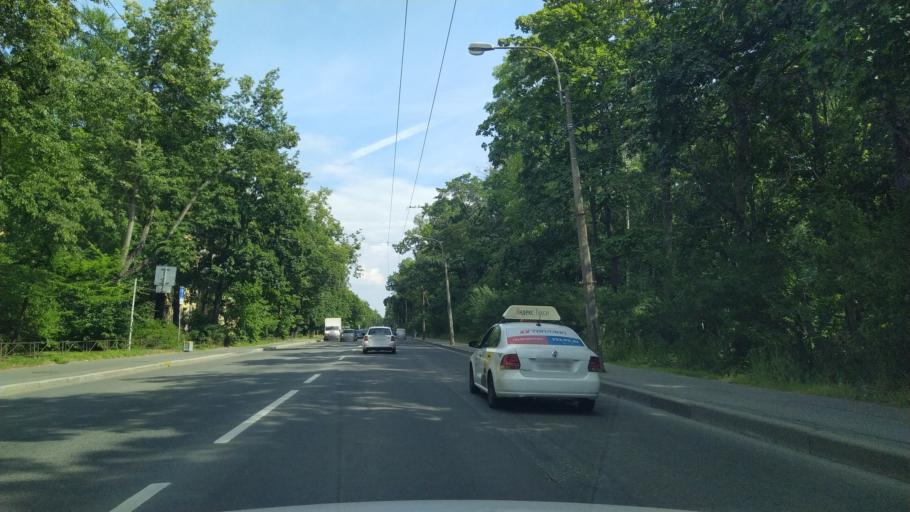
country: RU
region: Leningrad
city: Svetlanovskiy
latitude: 59.9969
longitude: 30.3389
